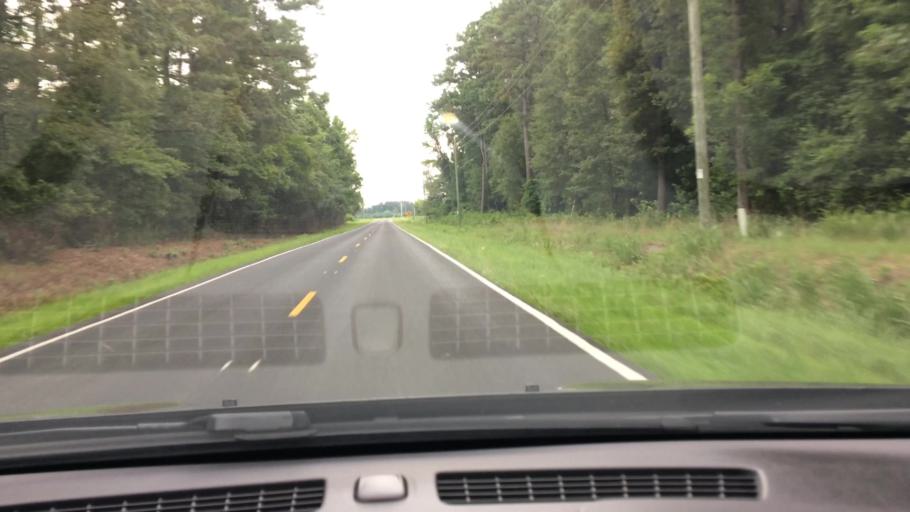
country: US
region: North Carolina
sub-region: Pitt County
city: Ayden
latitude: 35.4394
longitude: -77.4088
